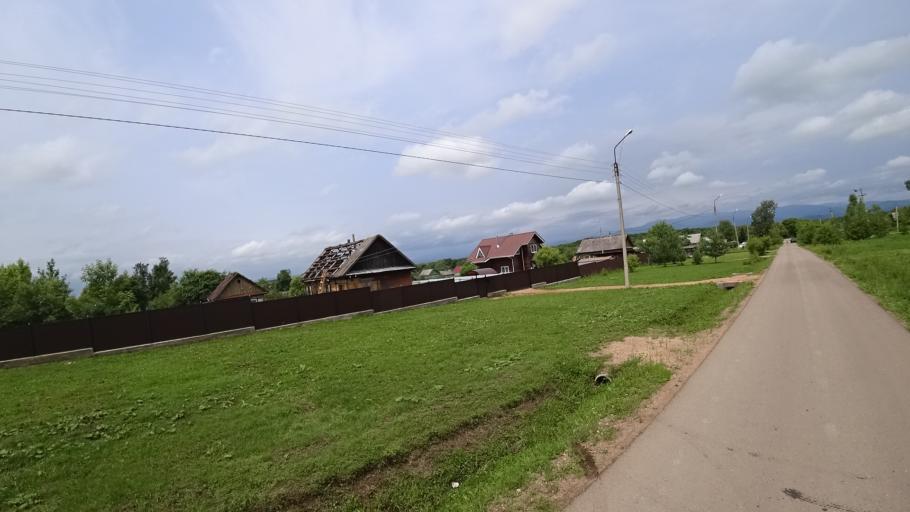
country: RU
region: Primorskiy
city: Novosysoyevka
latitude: 44.2365
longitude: 133.3587
